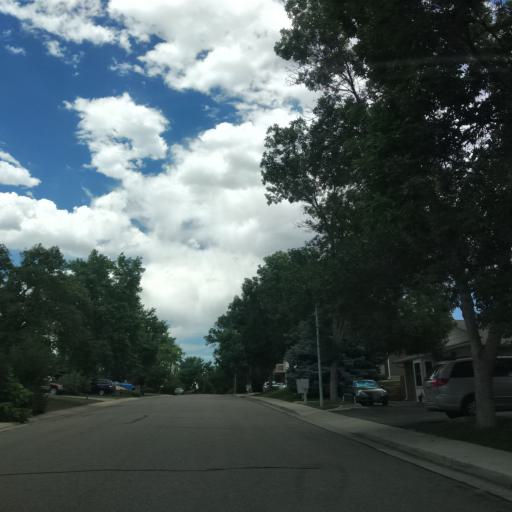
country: US
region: Colorado
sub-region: Jefferson County
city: Lakewood
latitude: 39.6845
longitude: -105.0873
